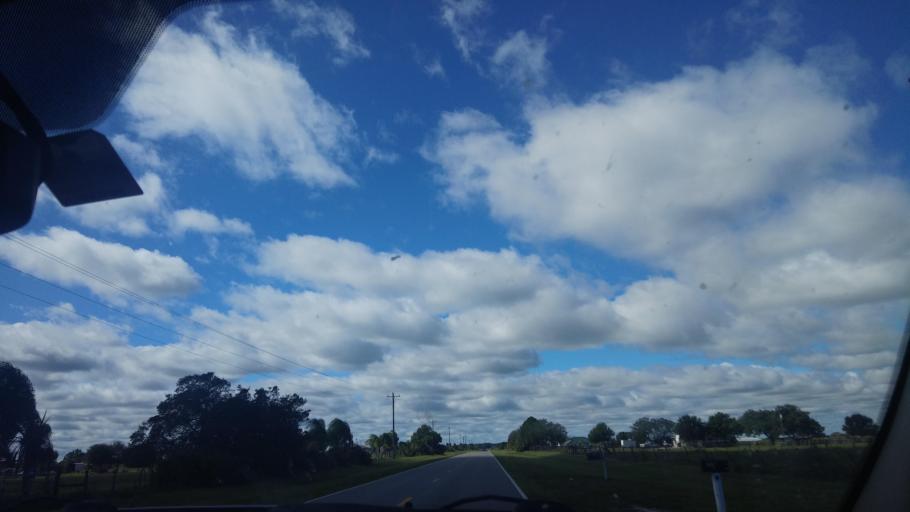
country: US
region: Florida
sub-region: Okeechobee County
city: Cypress Quarters
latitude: 27.3904
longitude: -80.8366
